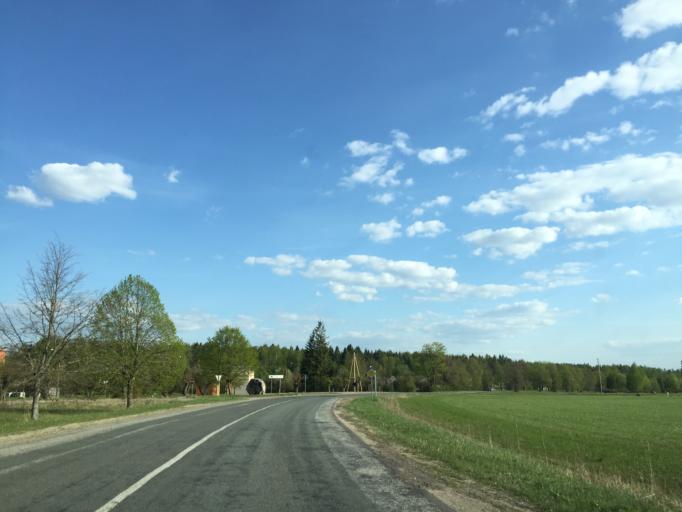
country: LV
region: Sigulda
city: Sigulda
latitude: 57.2558
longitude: 24.8736
